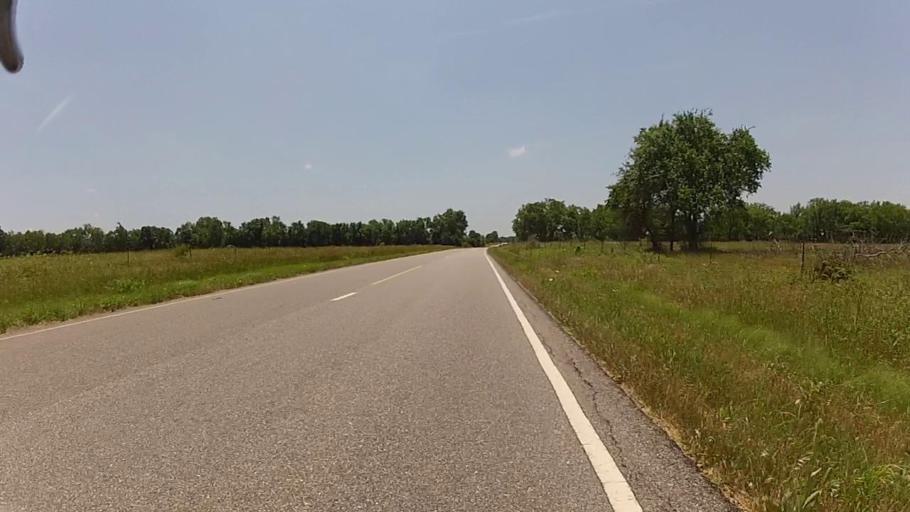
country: US
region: Kansas
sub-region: Montgomery County
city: Cherryvale
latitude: 37.2022
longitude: -95.5389
